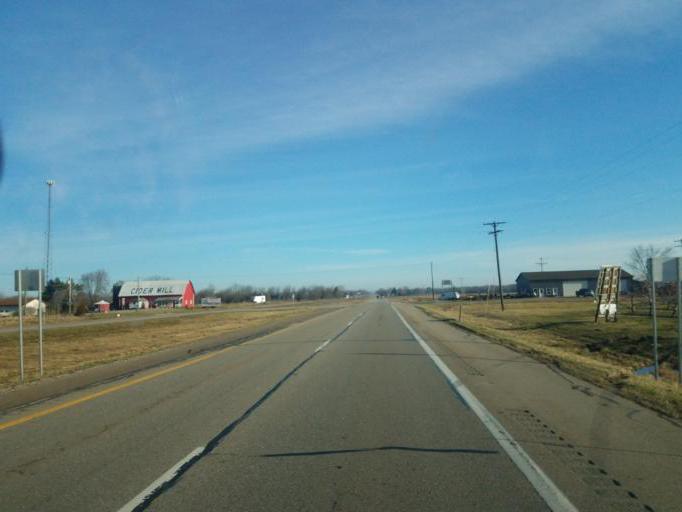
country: US
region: Michigan
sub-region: Clinton County
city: Saint Johns
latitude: 43.1167
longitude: -84.5631
